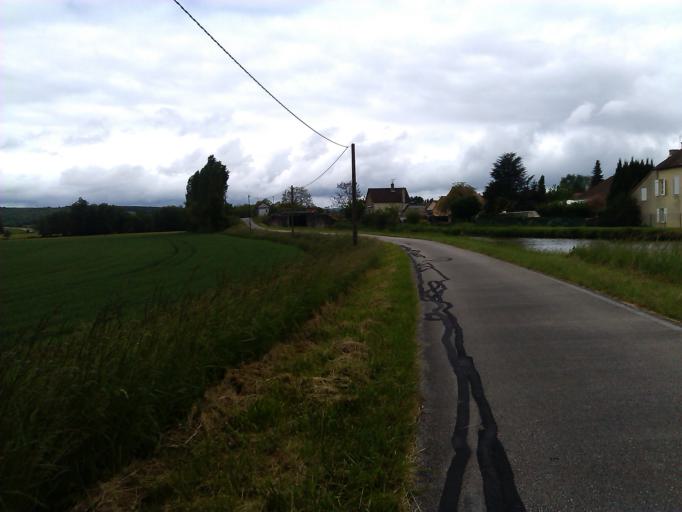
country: FR
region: Bourgogne
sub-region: Departement de Saone-et-Loire
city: Fontaines
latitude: 46.8776
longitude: 4.7726
